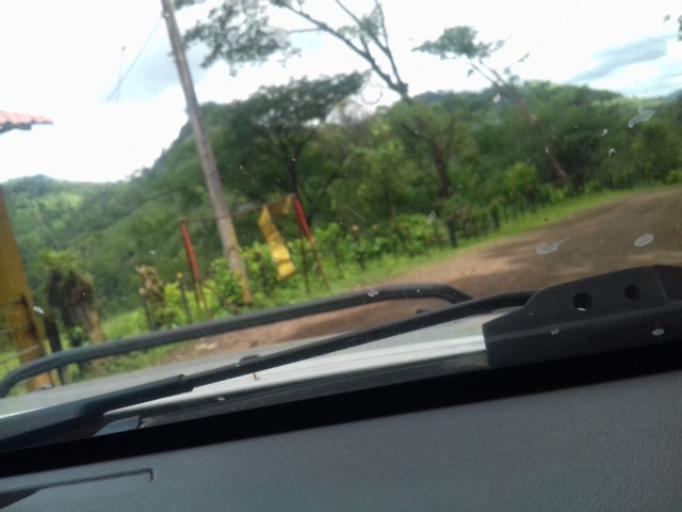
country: NI
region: Matagalpa
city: Rio Blanco
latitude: 13.0315
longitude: -85.2274
